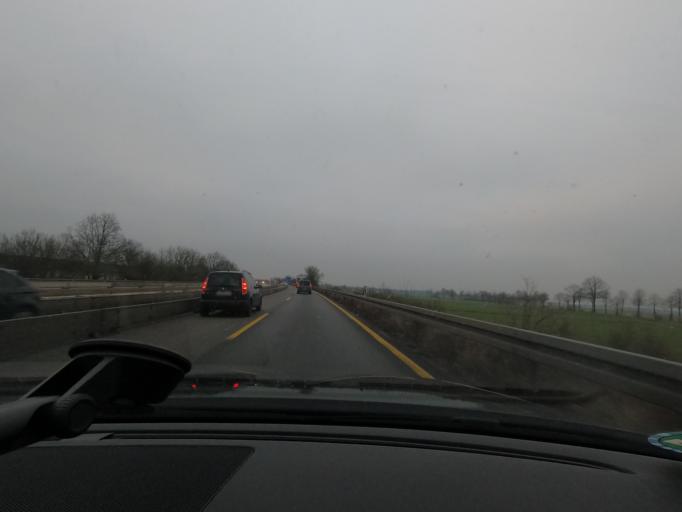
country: DE
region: North Rhine-Westphalia
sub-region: Regierungsbezirk Dusseldorf
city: Willich
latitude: 51.2811
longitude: 6.5099
